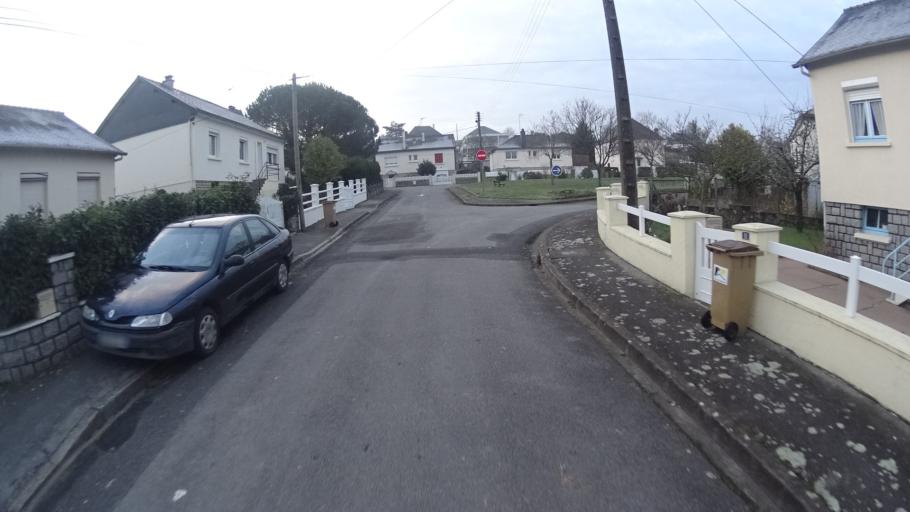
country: FR
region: Pays de la Loire
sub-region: Departement de la Loire-Atlantique
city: Saint-Nicolas-de-Redon
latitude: 47.6461
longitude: -2.0619
